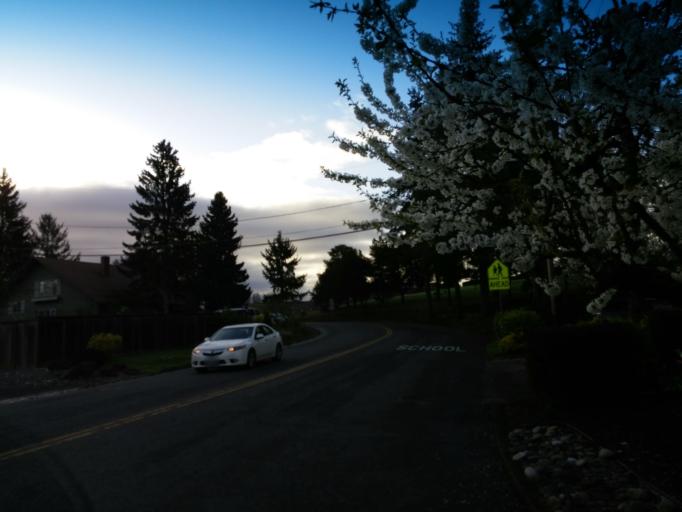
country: US
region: Oregon
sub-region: Washington County
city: Cedar Mill
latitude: 45.5085
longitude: -122.8191
